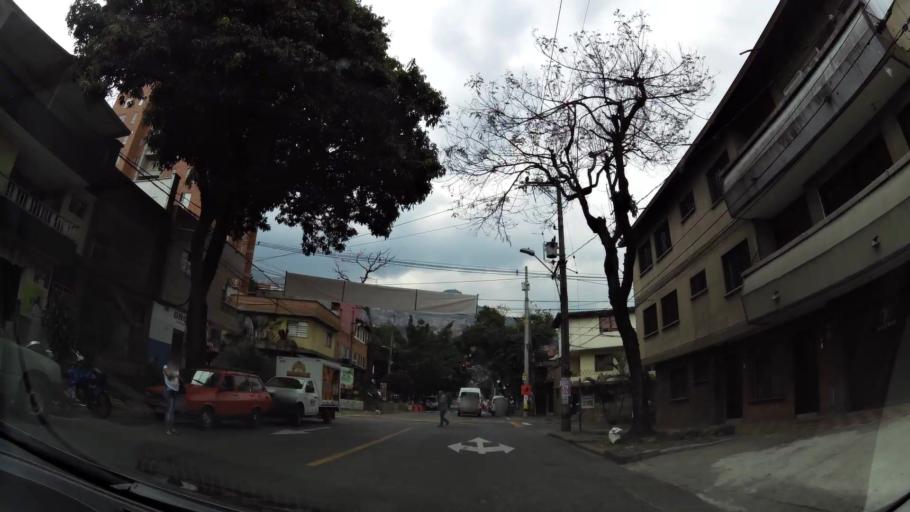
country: CO
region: Antioquia
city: Medellin
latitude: 6.2499
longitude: -75.5555
